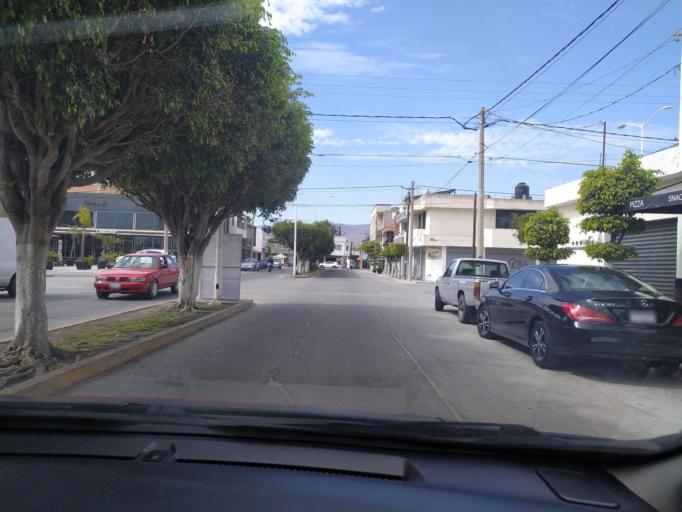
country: LA
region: Oudomxai
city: Muang La
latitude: 21.0125
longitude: 101.8578
